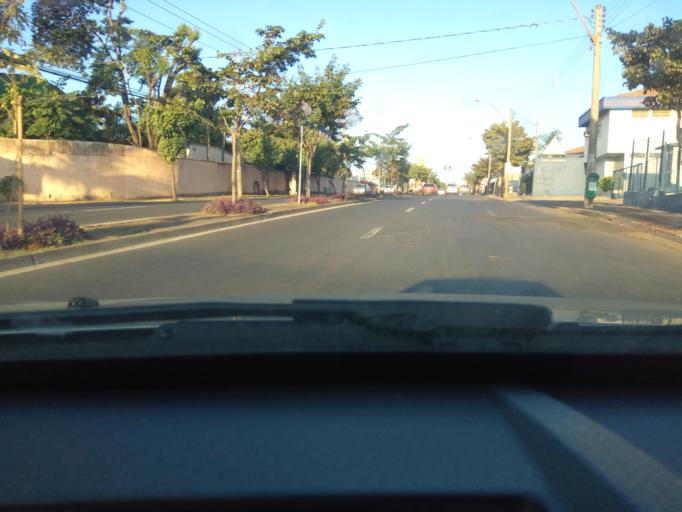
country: BR
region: Sao Paulo
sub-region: Piracicaba
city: Piracicaba
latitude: -22.7336
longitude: -47.6588
